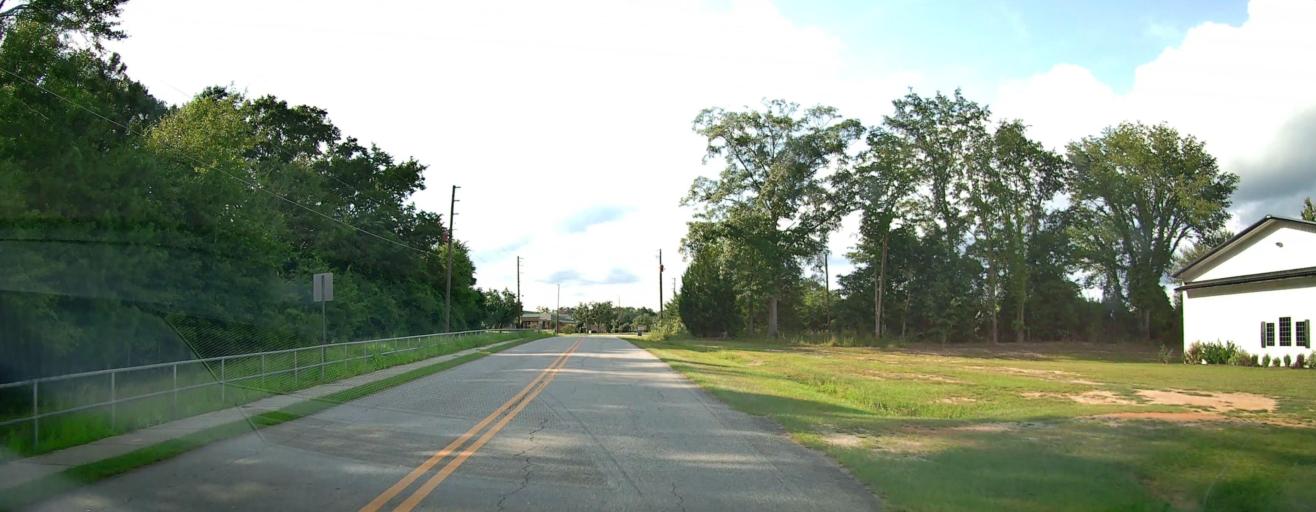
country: US
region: Georgia
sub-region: Crawford County
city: Roberta
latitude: 32.7265
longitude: -84.0063
